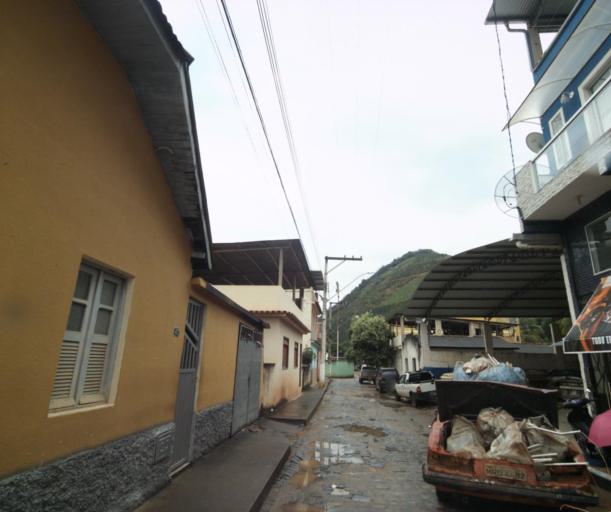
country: BR
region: Espirito Santo
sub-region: Muniz Freire
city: Muniz Freire
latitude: -20.4617
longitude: -41.4155
